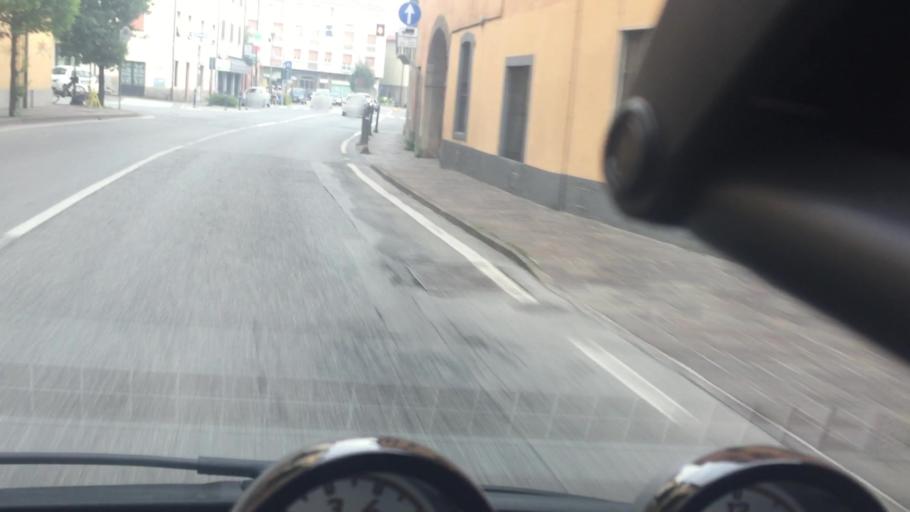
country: IT
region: Lombardy
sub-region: Provincia di Bergamo
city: Boltiere
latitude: 45.6008
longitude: 9.5797
